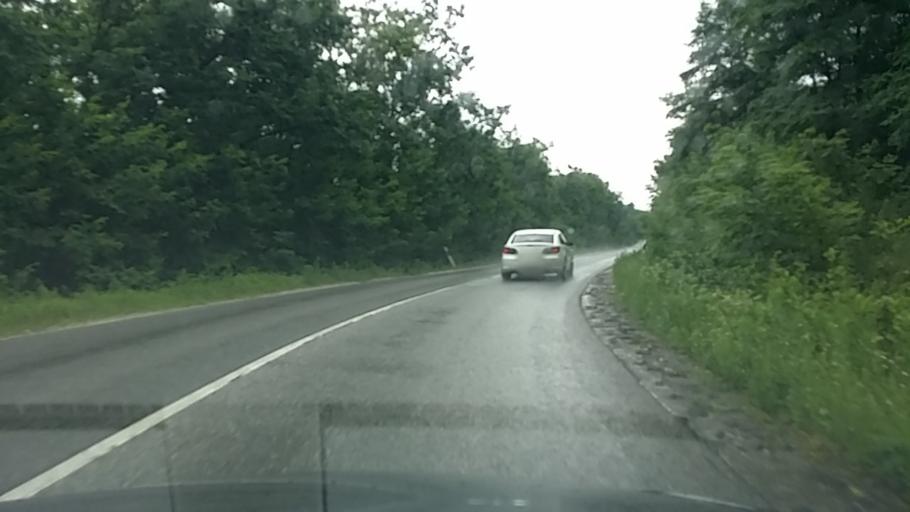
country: HU
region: Pest
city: Vecses
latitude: 47.3501
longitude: 19.3071
